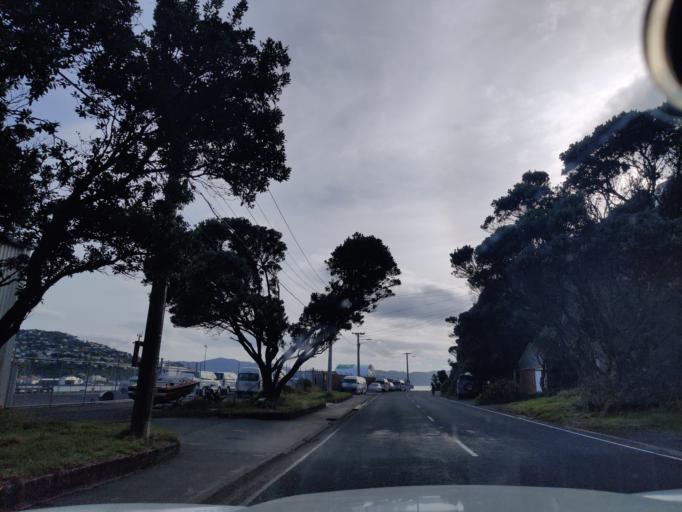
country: NZ
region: Wellington
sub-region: Wellington City
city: Wellington
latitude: -41.3117
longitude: 174.8124
